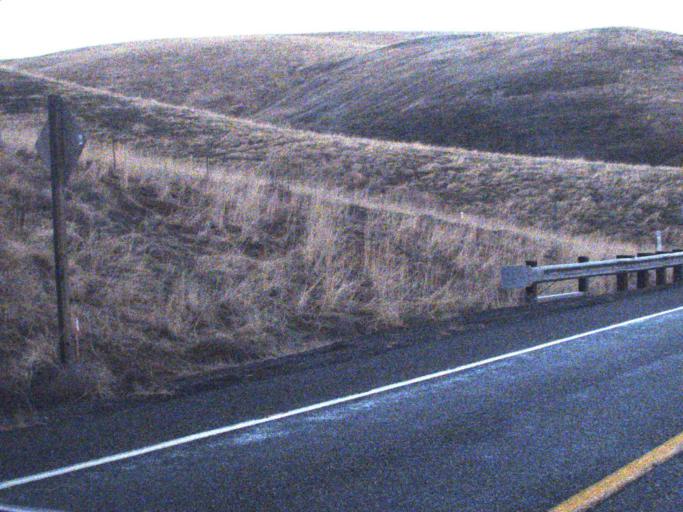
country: US
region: Washington
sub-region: Garfield County
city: Pomeroy
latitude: 46.5938
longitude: -117.7821
